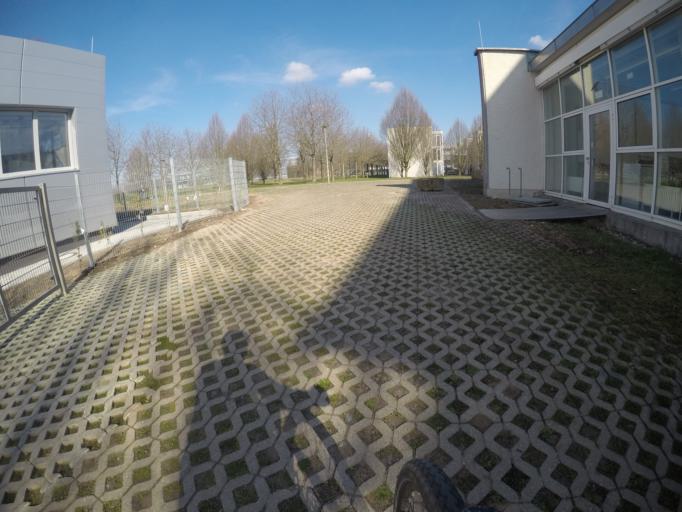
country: DE
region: Baden-Wuerttemberg
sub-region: Regierungsbezirk Stuttgart
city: Gerlingen
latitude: 48.7421
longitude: 9.1001
